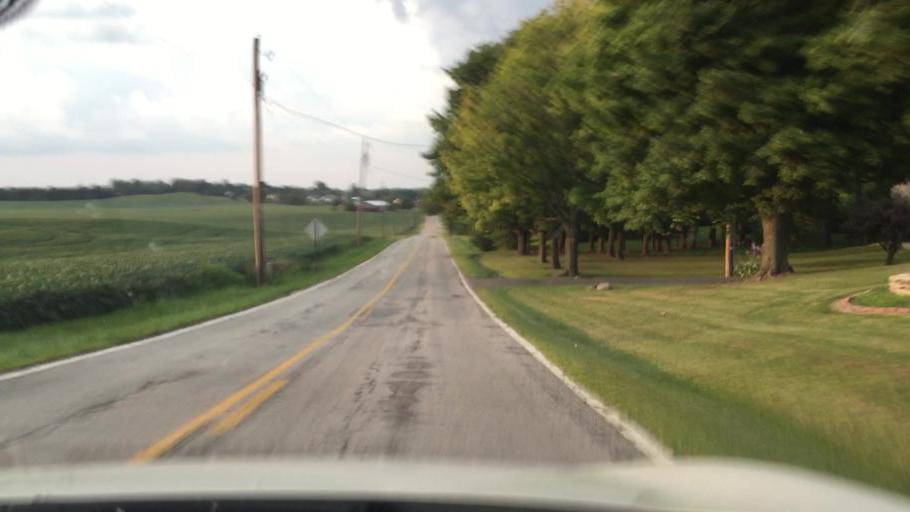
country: US
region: Ohio
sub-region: Champaign County
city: Mechanicsburg
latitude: 40.0116
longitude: -83.5918
